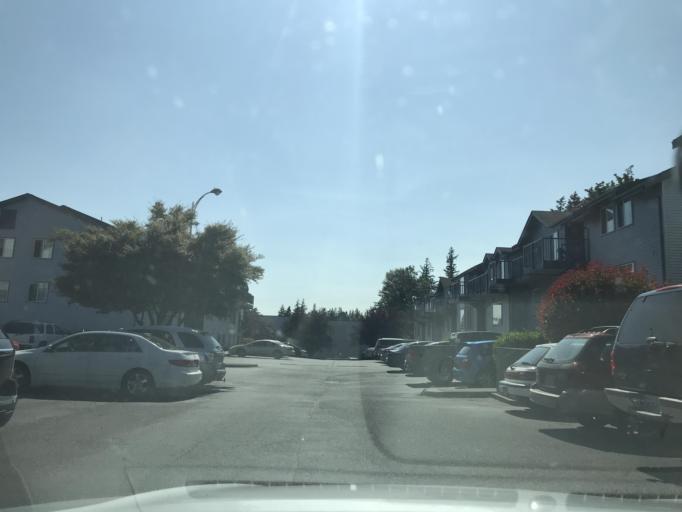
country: US
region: Washington
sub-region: Whatcom County
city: Bellingham
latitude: 48.7766
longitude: -122.4921
